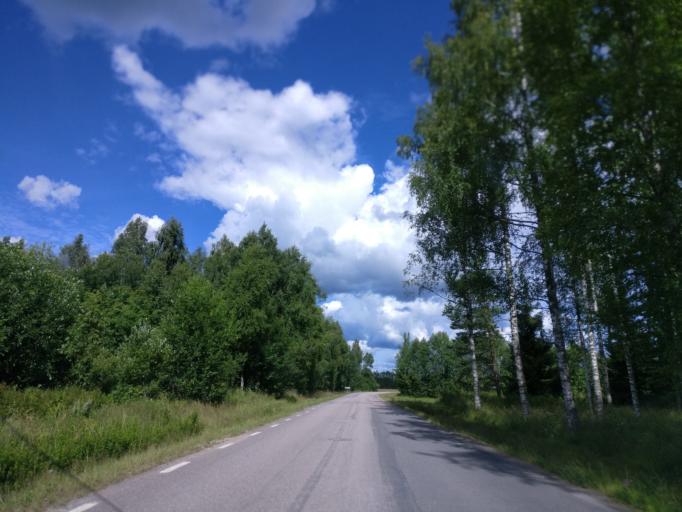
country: SE
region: Vaermland
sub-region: Hagfors Kommun
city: Ekshaerad
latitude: 60.0416
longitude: 13.4947
